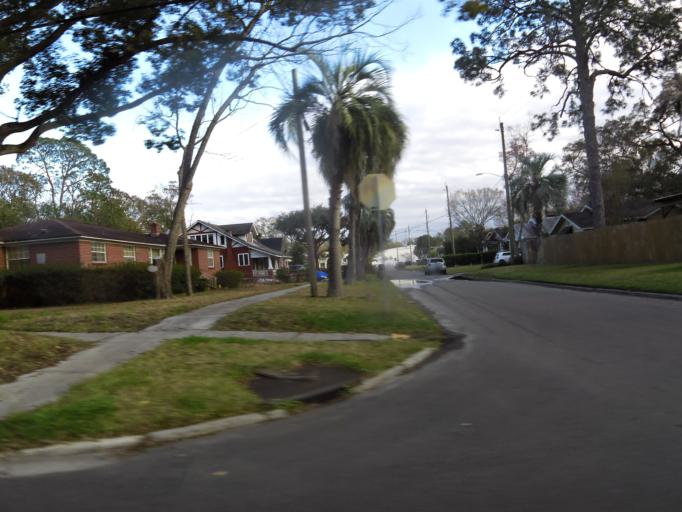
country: US
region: Florida
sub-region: Duval County
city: Jacksonville
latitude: 30.3086
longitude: -81.7173
